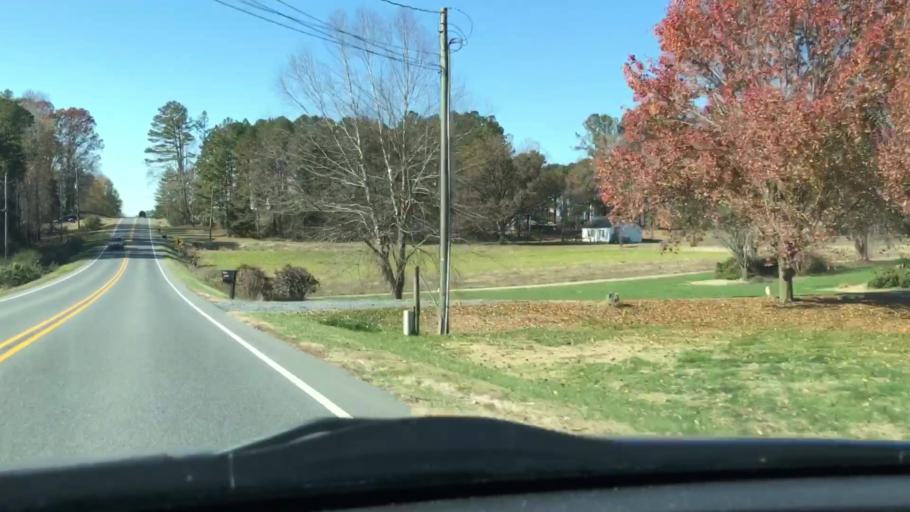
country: US
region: North Carolina
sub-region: Randolph County
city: Asheboro
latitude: 35.6742
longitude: -79.8947
